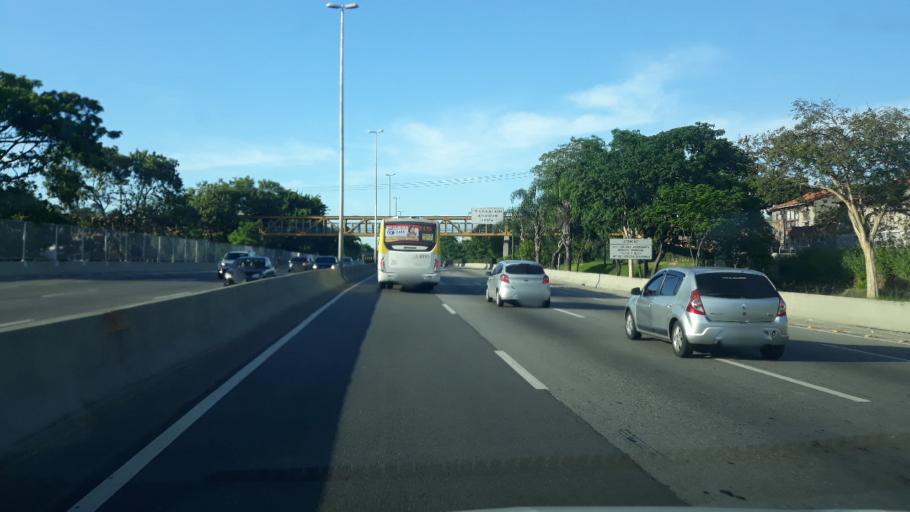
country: BR
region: Rio de Janeiro
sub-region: Sao Joao De Meriti
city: Sao Joao de Meriti
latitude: -22.9427
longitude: -43.3526
